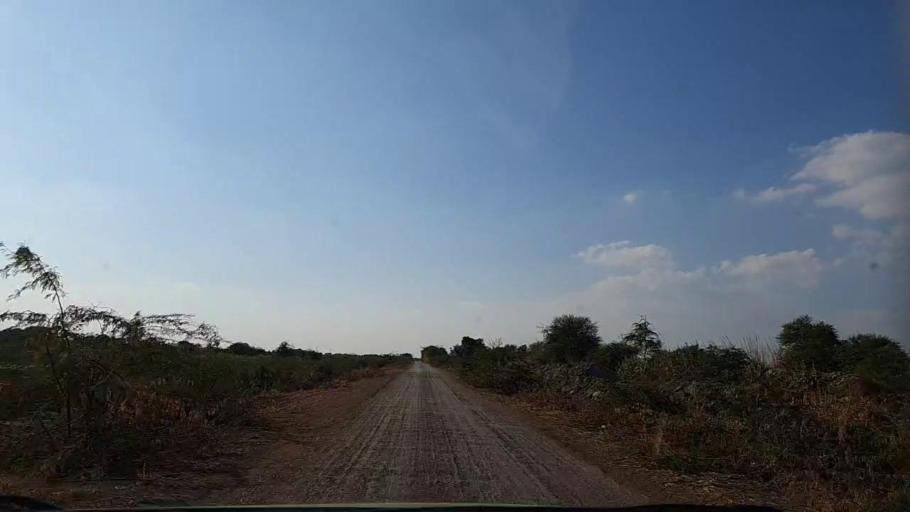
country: PK
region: Sindh
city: Pithoro
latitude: 25.6466
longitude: 69.3382
